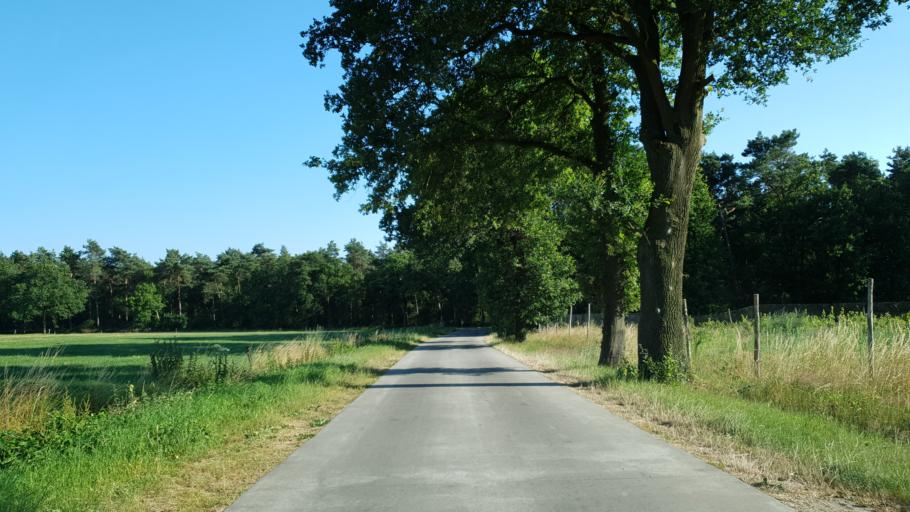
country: BE
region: Flanders
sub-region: Provincie Antwerpen
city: Merksplas
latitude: 51.4036
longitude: 4.8369
